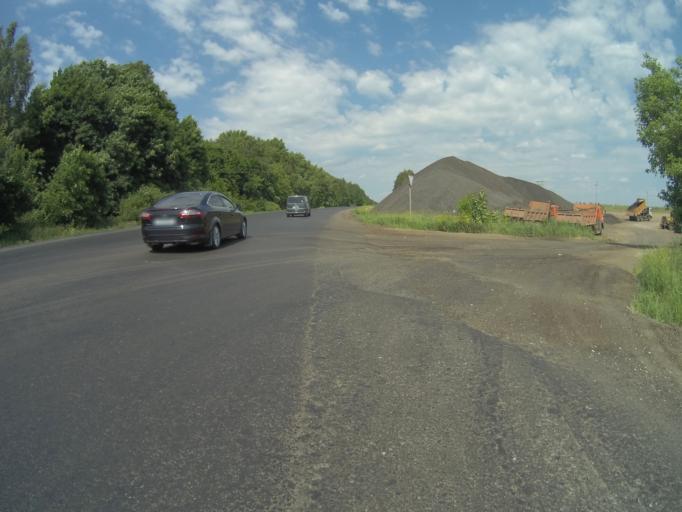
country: RU
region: Vladimir
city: Bogolyubovo
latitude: 56.2248
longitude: 40.4427
